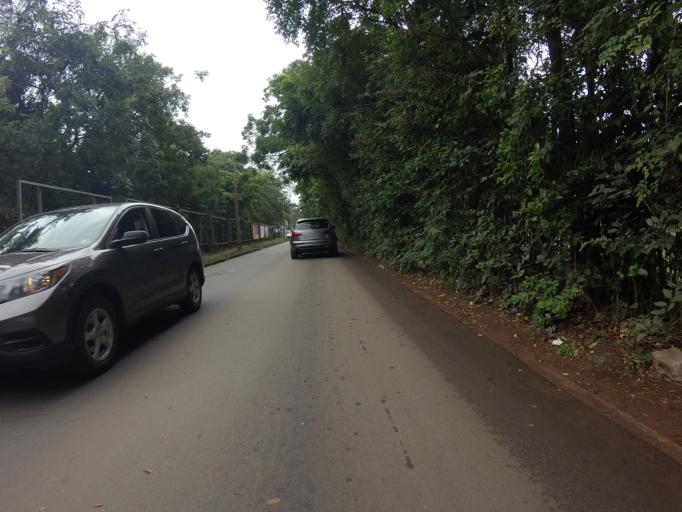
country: GH
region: Greater Accra
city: Dome
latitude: 5.6282
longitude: -0.2198
